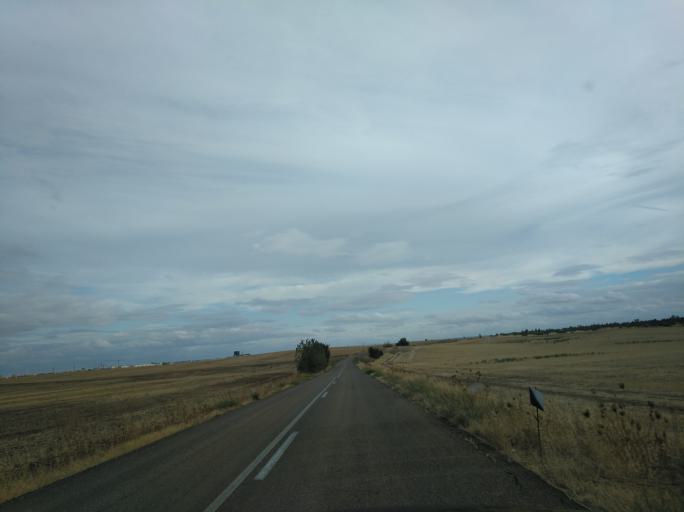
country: ES
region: Extremadura
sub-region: Provincia de Badajoz
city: Badajoz
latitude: 38.9027
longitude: -7.0178
